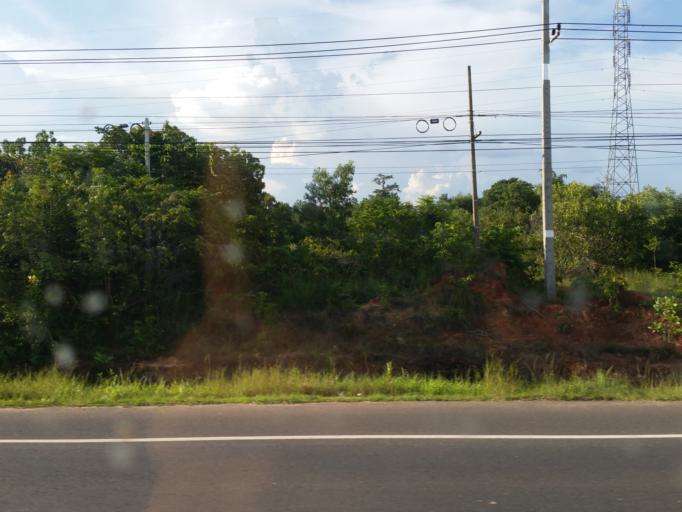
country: TH
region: Changwat Ubon Ratchathani
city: Sirindhorn
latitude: 15.2010
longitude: 105.3800
